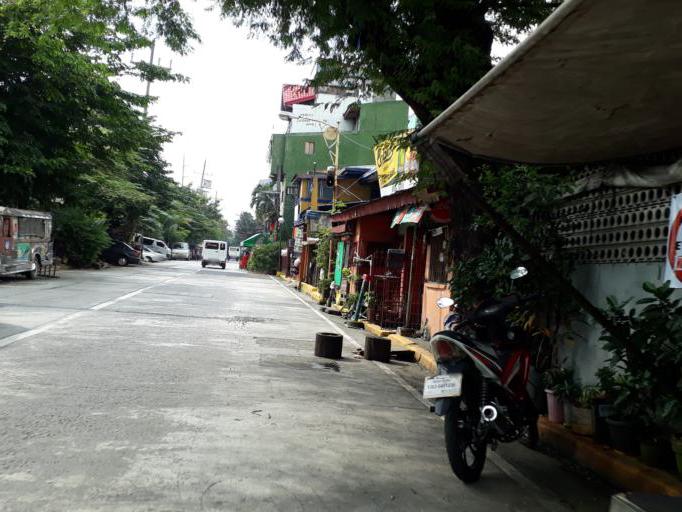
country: PH
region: Metro Manila
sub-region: City of Manila
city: Manila
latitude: 14.6089
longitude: 121.0003
